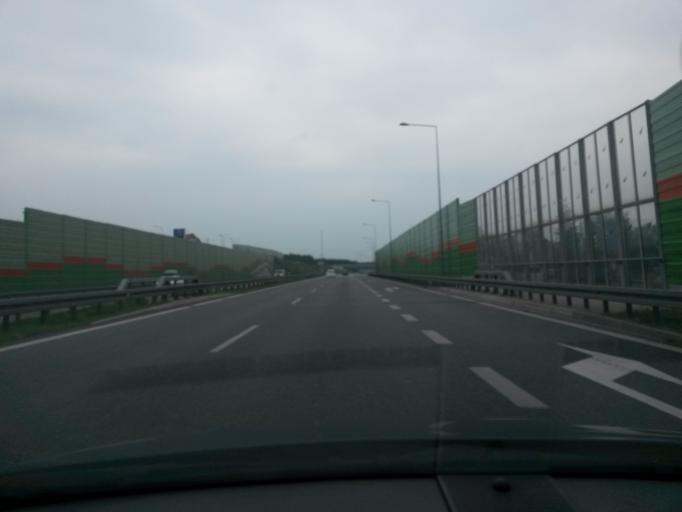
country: PL
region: Lodz Voivodeship
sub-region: Powiat tomaszowski
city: Tomaszow Mazowiecki
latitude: 51.5284
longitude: 19.9454
